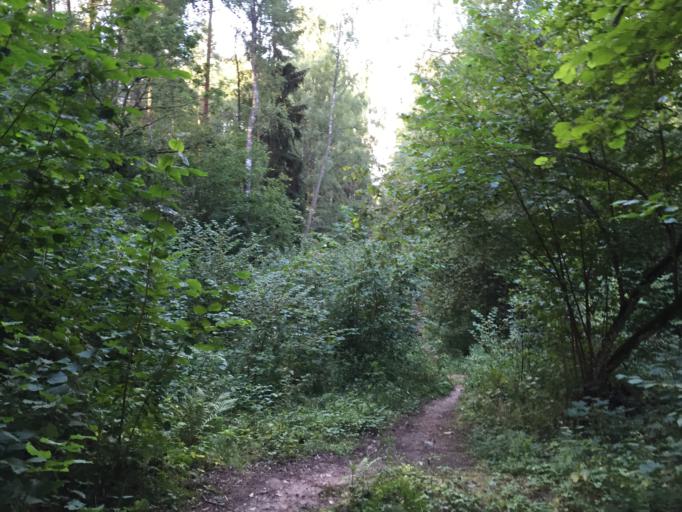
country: LV
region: Ikskile
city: Ikskile
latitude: 56.8411
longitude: 24.5403
